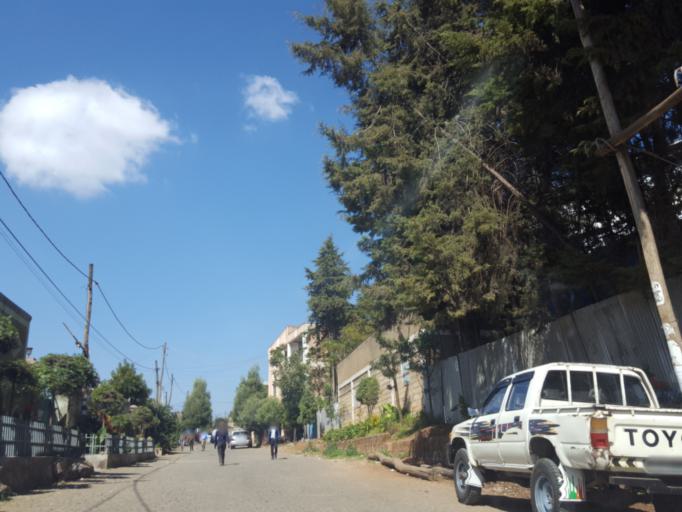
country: ET
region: Adis Abeba
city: Addis Ababa
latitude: 9.0595
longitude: 38.7343
